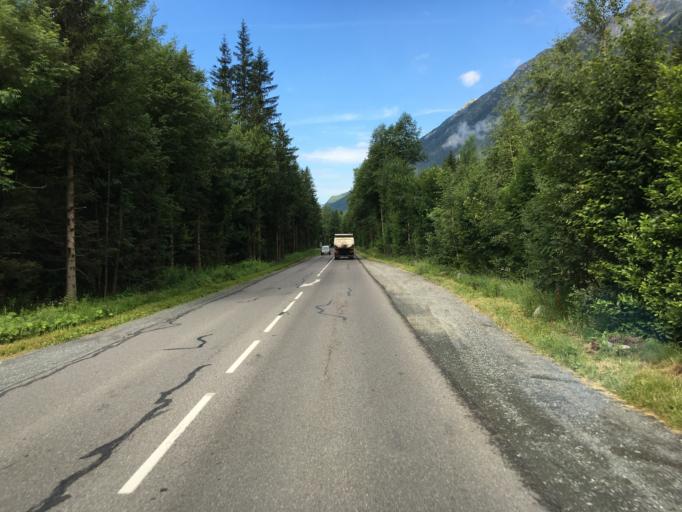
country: FR
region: Rhone-Alpes
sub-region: Departement de la Haute-Savoie
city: Chamonix-Mont-Blanc
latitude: 45.9339
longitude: 6.8881
